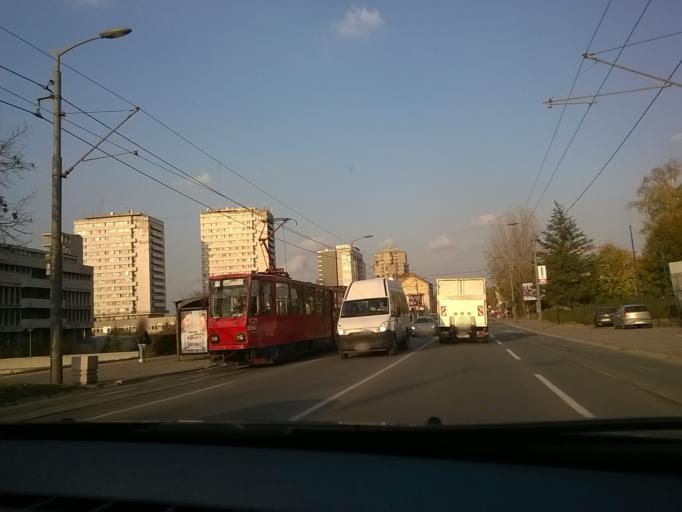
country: RS
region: Central Serbia
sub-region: Belgrade
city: Vracar
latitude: 44.8119
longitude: 20.4879
